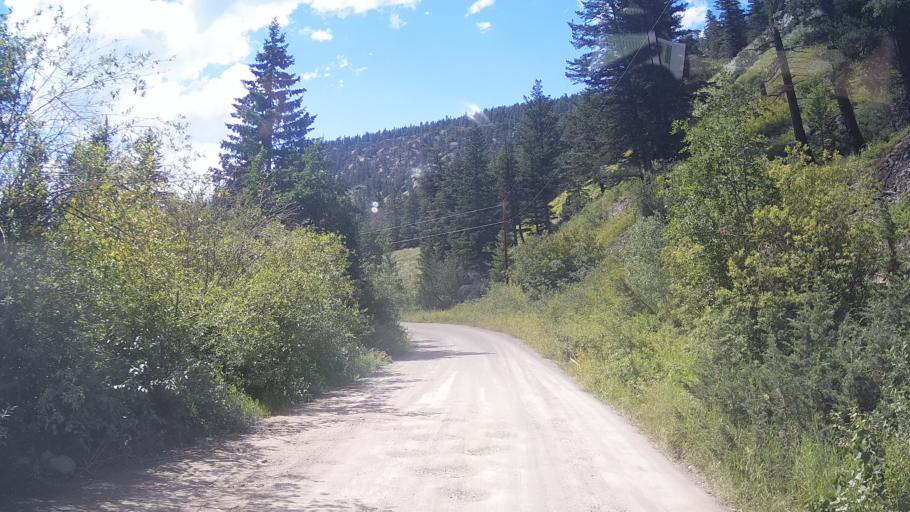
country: CA
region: British Columbia
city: Lillooet
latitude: 51.2557
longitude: -122.0033
